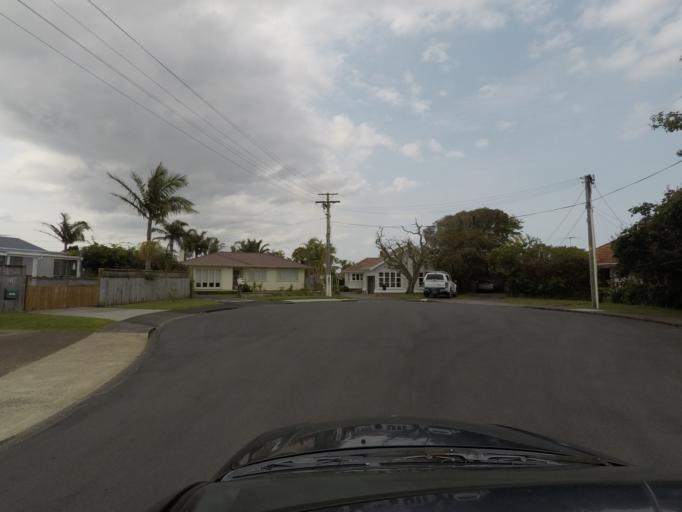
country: NZ
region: Auckland
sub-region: Auckland
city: Rosebank
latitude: -36.8300
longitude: 174.6453
